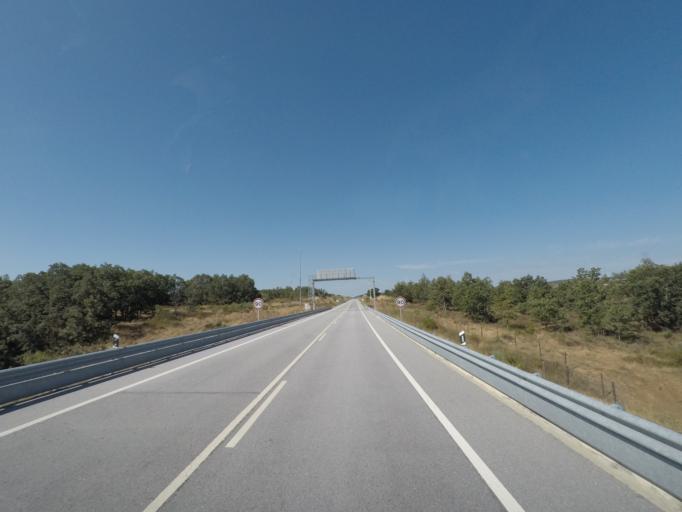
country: ES
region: Castille and Leon
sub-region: Provincia de Salamanca
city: Villarino de los Aires
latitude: 41.3628
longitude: -6.5307
